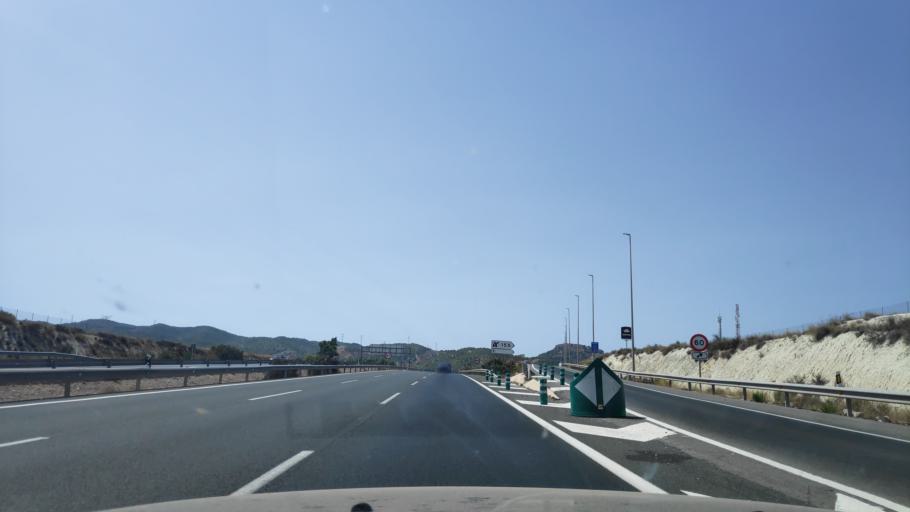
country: ES
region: Murcia
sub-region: Murcia
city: Murcia
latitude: 37.8820
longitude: -1.1339
